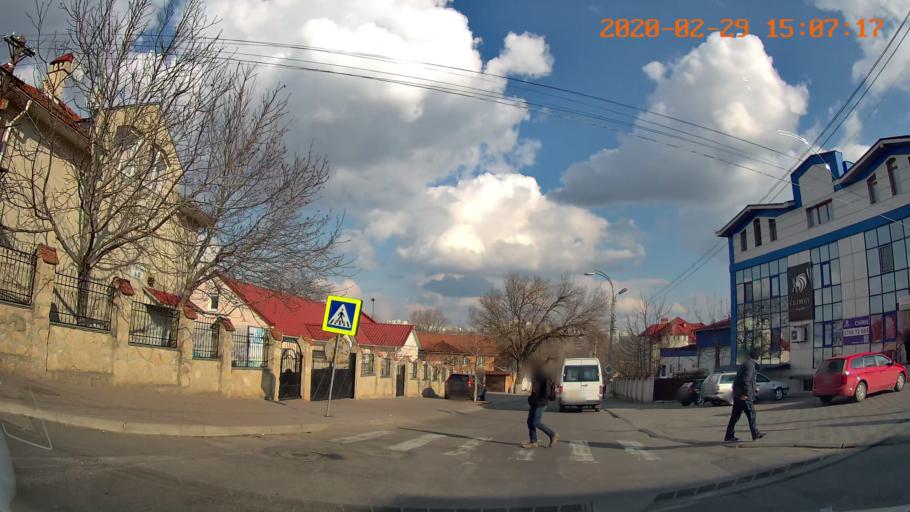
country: MD
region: Chisinau
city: Chisinau
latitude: 47.0521
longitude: 28.8458
